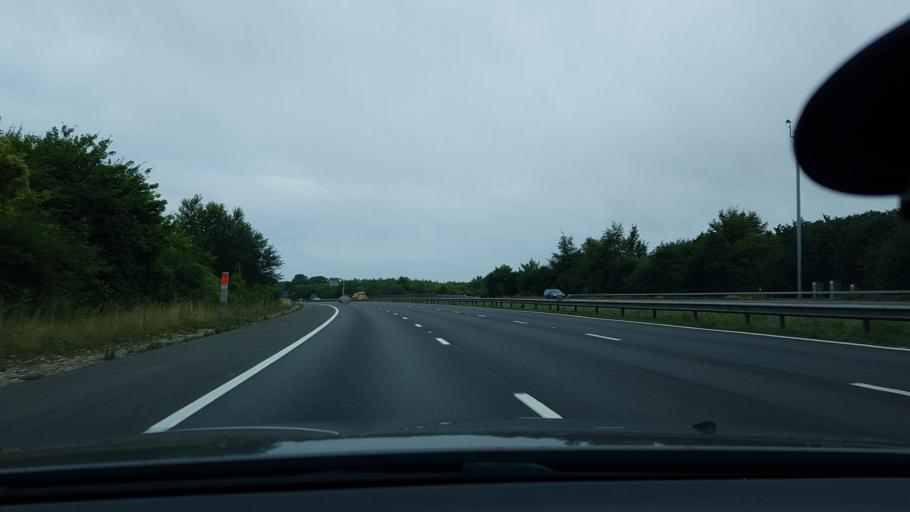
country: GB
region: England
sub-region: Hampshire
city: Compton
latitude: 51.0345
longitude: -1.3239
